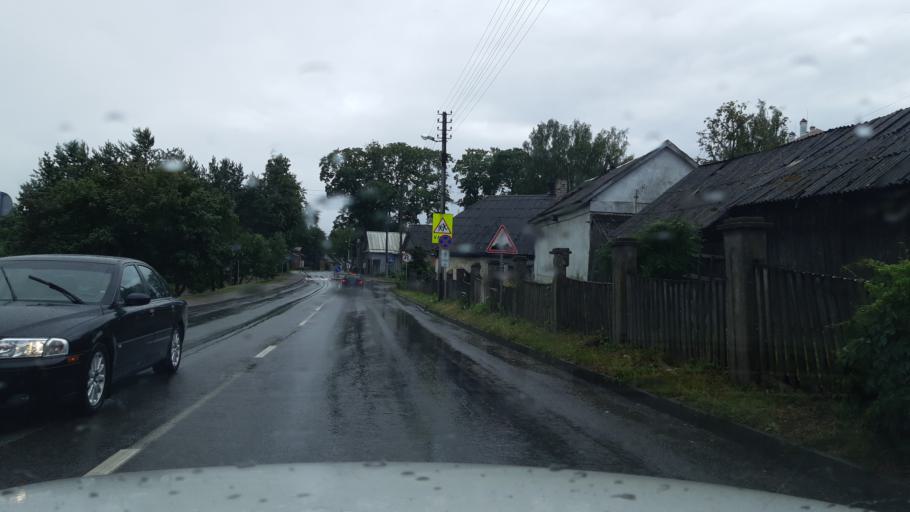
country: LT
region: Taurages apskritis
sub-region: Jurbarkas
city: Jurbarkas
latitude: 55.0798
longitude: 22.7599
